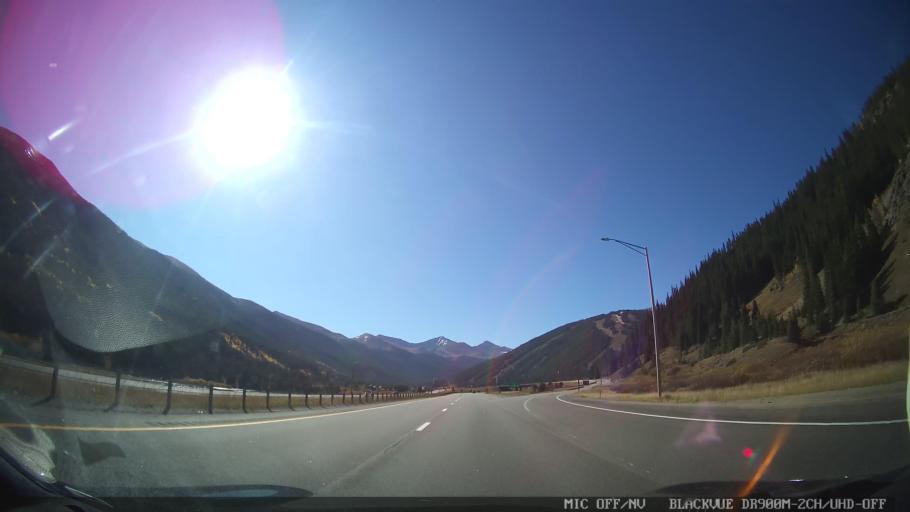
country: US
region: Colorado
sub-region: Summit County
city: Frisco
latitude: 39.5126
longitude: -106.1449
